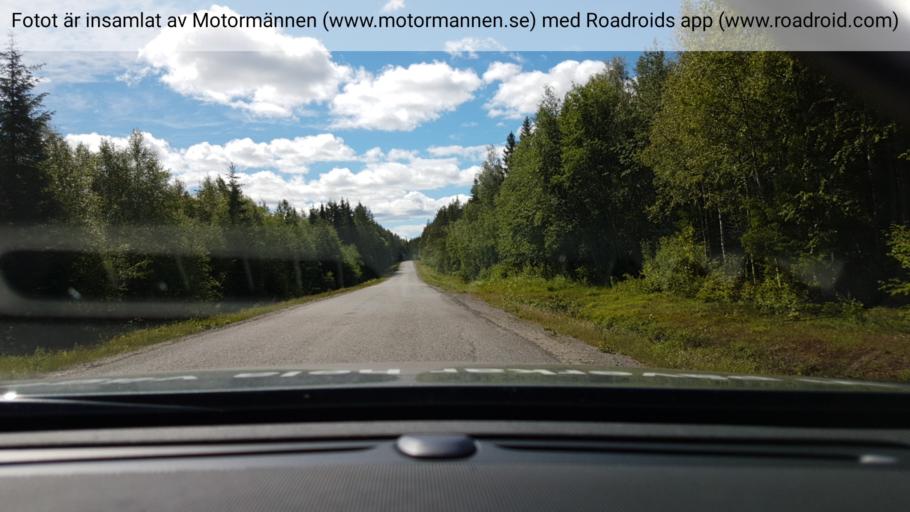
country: SE
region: Vaesterbotten
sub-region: Skelleftea Kommun
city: Burea
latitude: 64.4072
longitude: 21.3474
